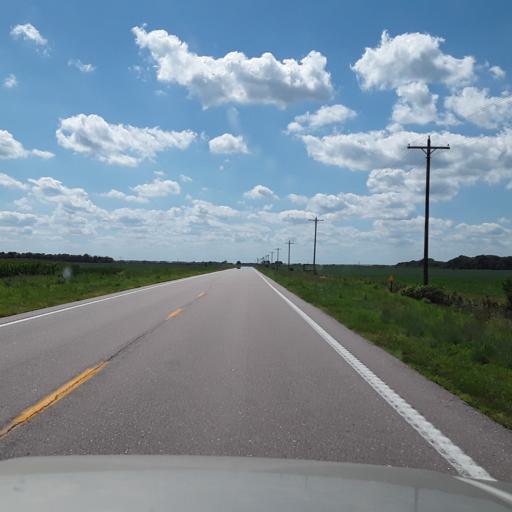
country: US
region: Nebraska
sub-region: Merrick County
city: Central City
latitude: 41.1913
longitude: -98.0470
